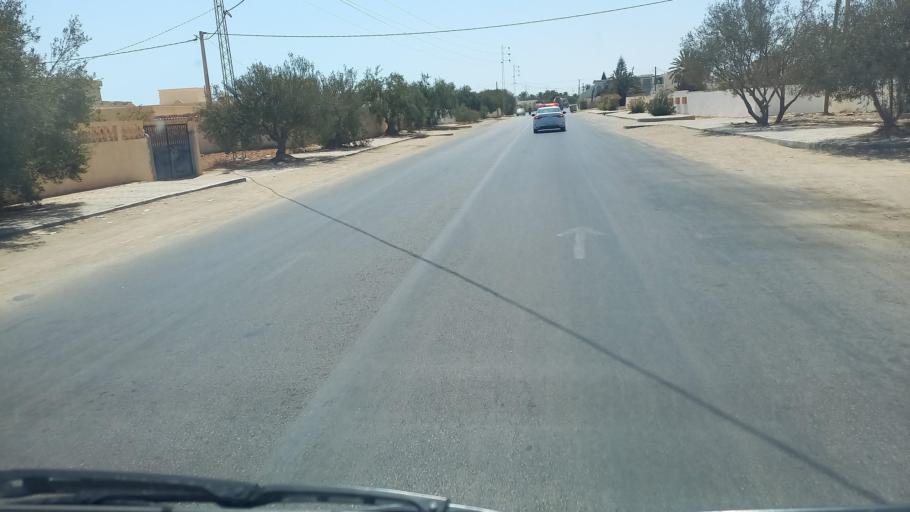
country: TN
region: Madanin
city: Houmt Souk
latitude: 33.7976
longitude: 10.8851
